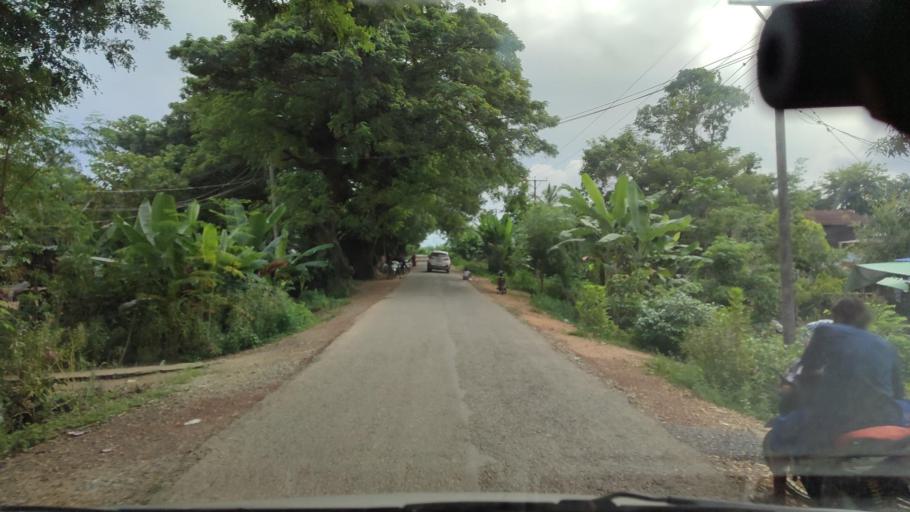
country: MM
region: Bago
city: Tharyarwady
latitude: 17.6336
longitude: 95.7512
